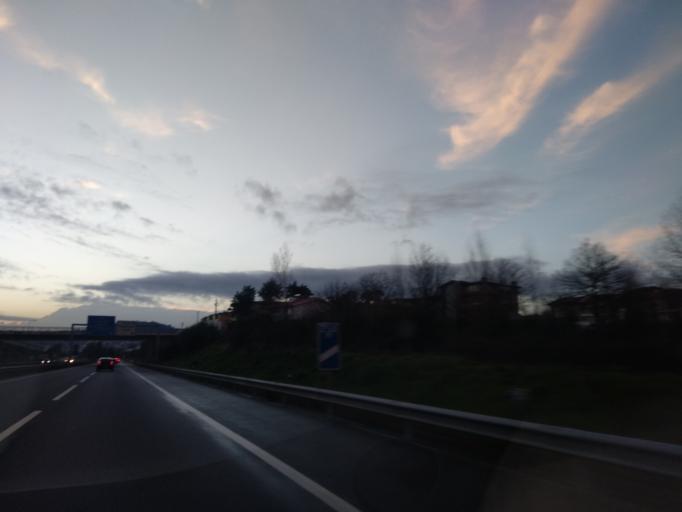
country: PT
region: Braga
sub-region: Vila Nova de Famalicao
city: Vila Nova de Famalicao
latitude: 41.3845
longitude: -8.5109
